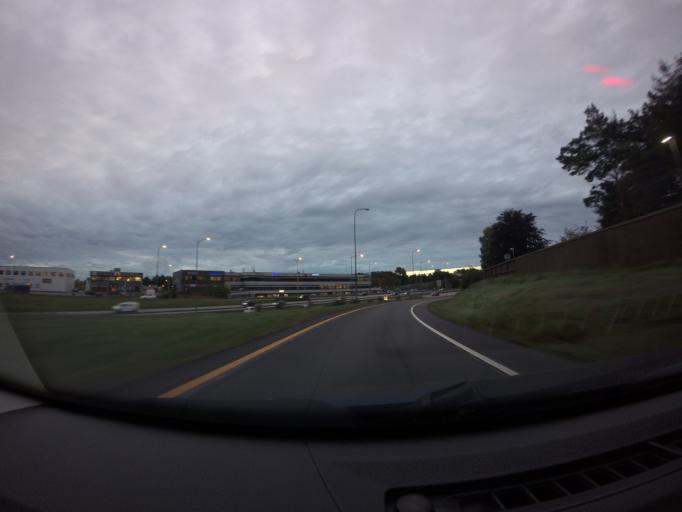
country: NO
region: Rogaland
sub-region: Stavanger
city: Stavanger
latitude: 58.9433
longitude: 5.7245
